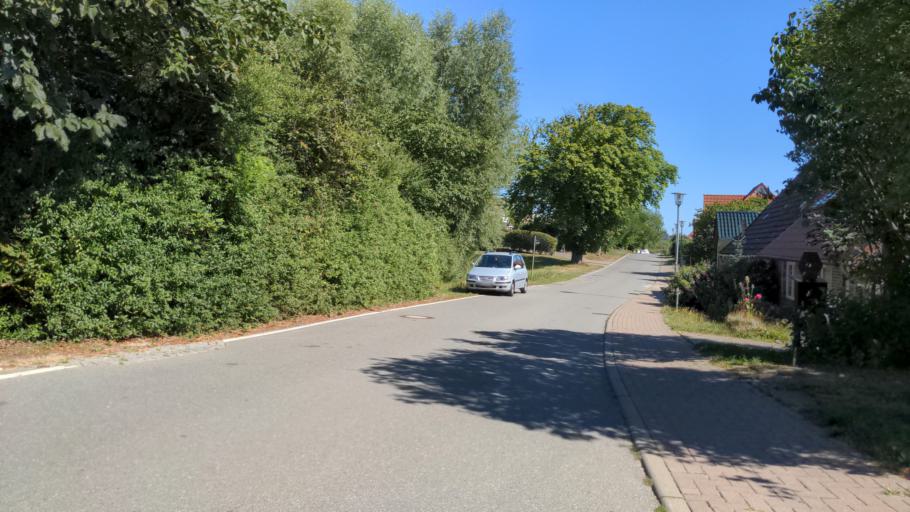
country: DE
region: Mecklenburg-Vorpommern
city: Ostseebad Boltenhagen
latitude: 53.9916
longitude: 11.1810
